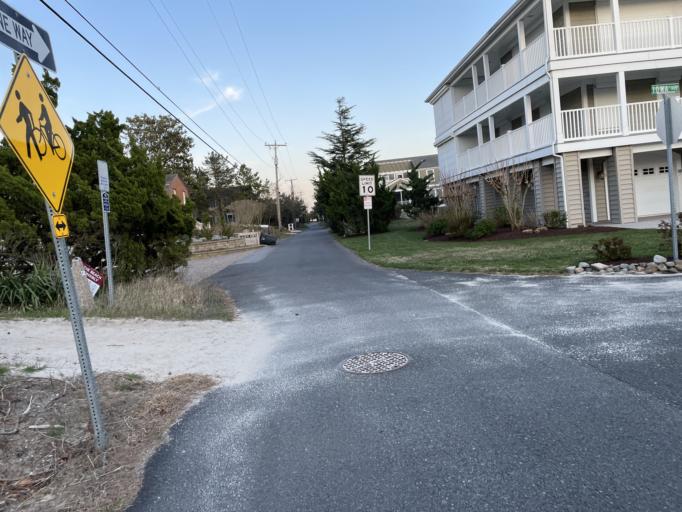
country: US
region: Delaware
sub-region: Sussex County
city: Lewes
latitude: 38.7880
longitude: -75.1556
